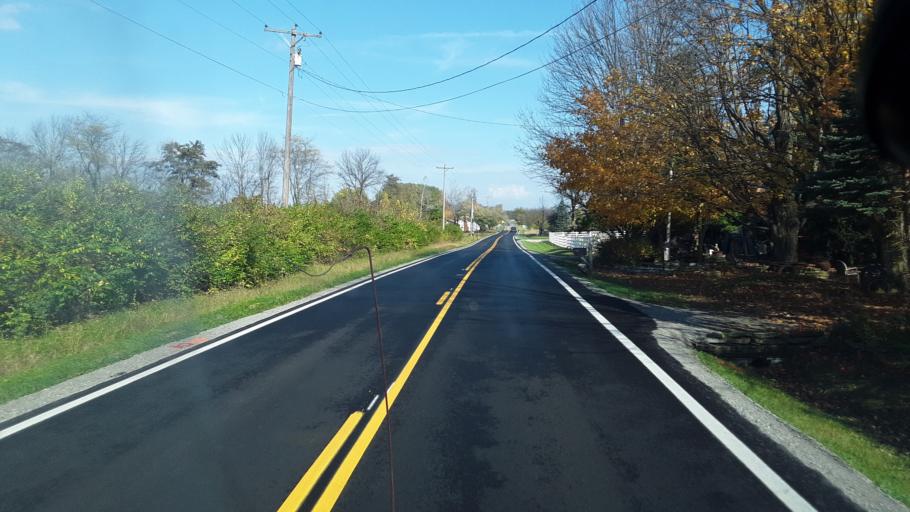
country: US
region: Ohio
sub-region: Highland County
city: Leesburg
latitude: 39.3739
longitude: -83.5937
